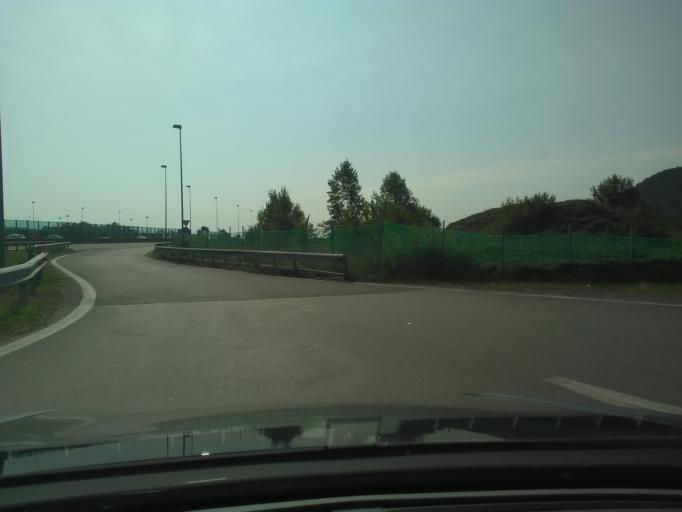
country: IT
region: Lombardy
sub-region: Provincia di Brescia
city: Erbusco
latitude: 45.5930
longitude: 9.9663
